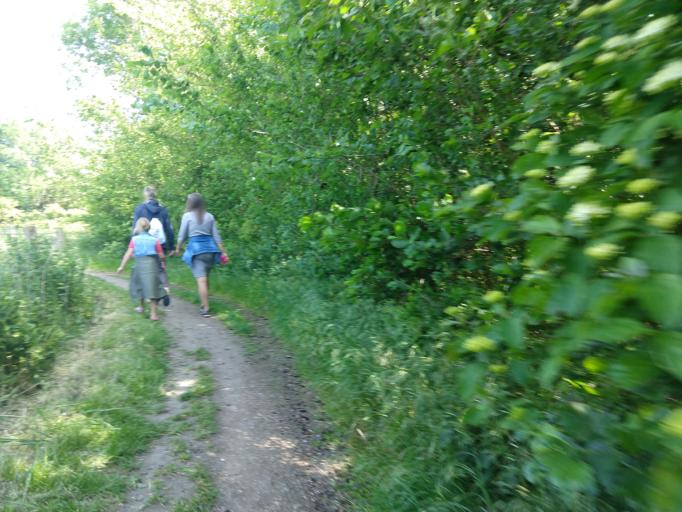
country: NL
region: Zeeland
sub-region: Gemeente Goes
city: Goes
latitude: 51.4443
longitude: 3.8706
